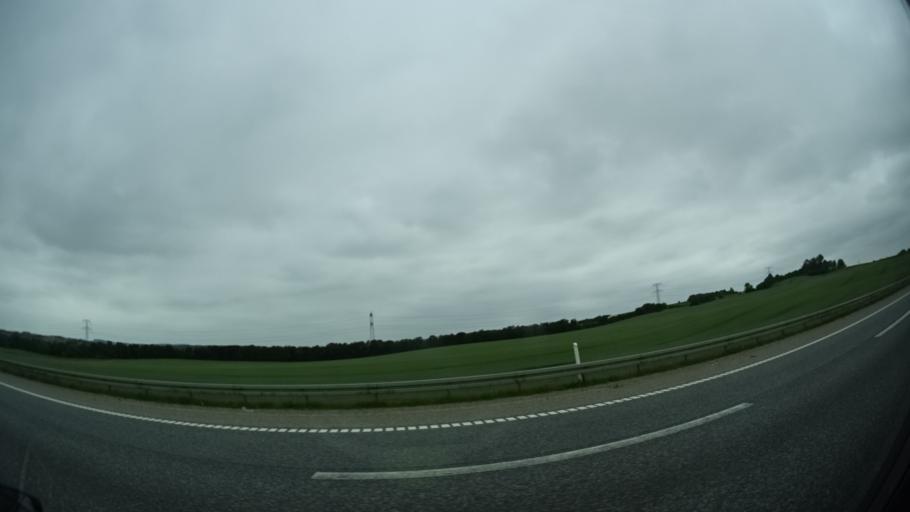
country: DK
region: Central Jutland
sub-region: Favrskov Kommune
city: Soften
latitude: 56.2204
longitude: 10.1136
